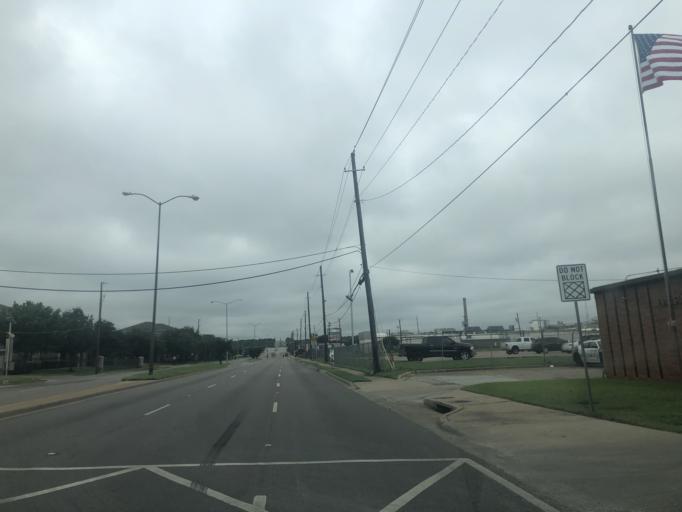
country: US
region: Texas
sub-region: Dallas County
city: Dallas
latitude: 32.7820
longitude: -96.8566
